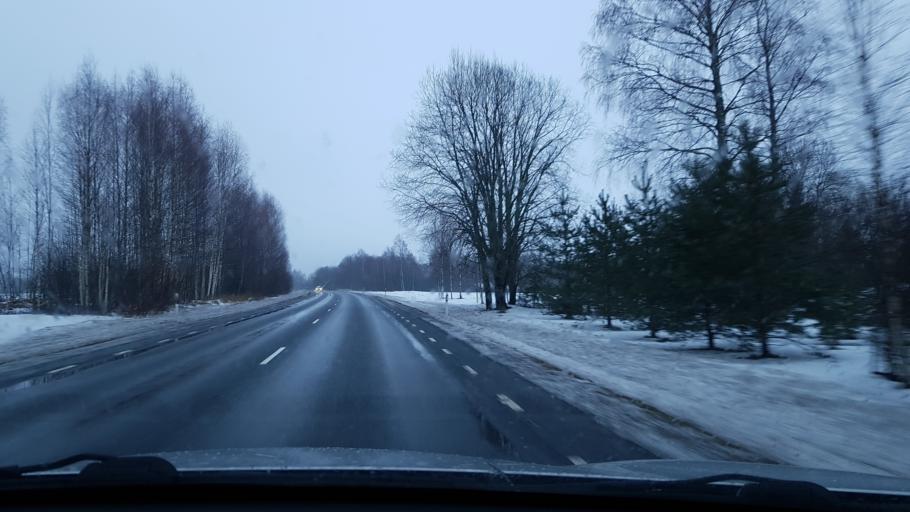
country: EE
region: Jaervamaa
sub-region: Tueri vald
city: Sarevere
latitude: 58.7997
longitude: 25.2413
